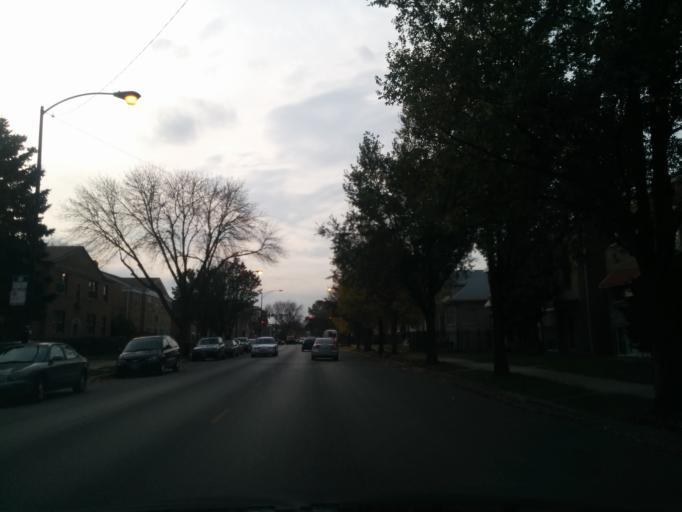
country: US
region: Illinois
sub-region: Cook County
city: Harwood Heights
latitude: 41.9460
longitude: -87.7553
